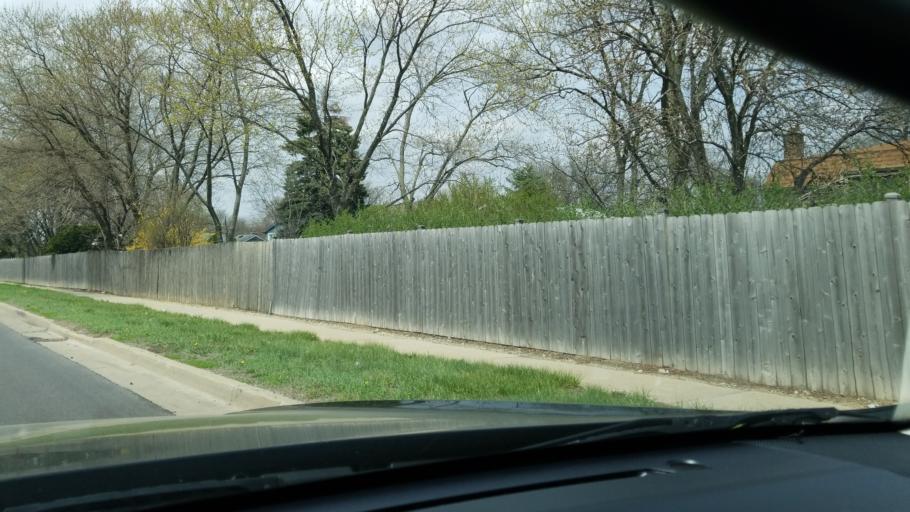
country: US
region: Illinois
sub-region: Cook County
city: Rolling Meadows
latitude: 42.0545
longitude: -87.9980
